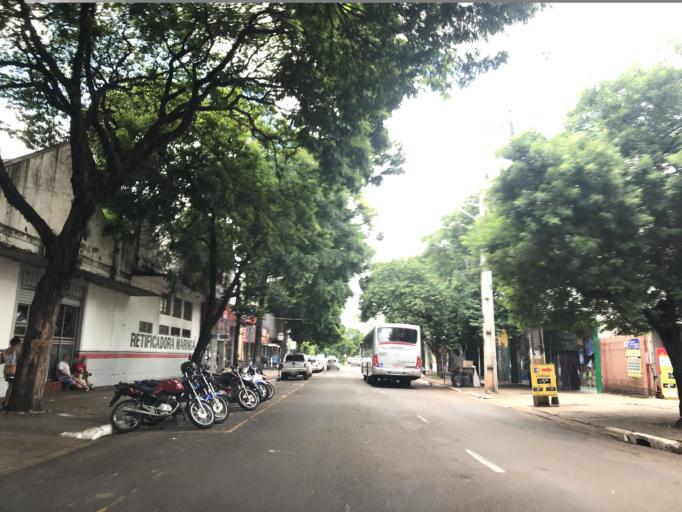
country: BR
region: Parana
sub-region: Maringa
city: Maringa
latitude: -23.4198
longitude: -51.9343
